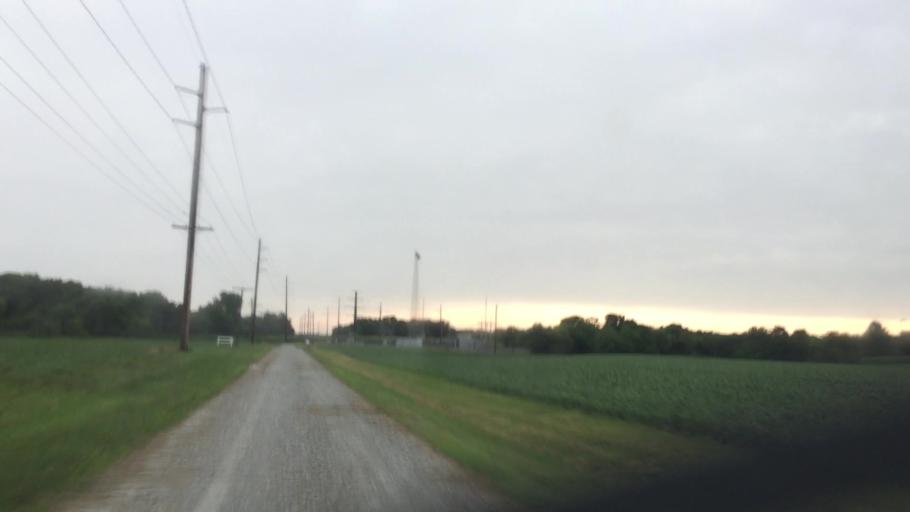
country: US
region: Iowa
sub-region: Lee County
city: Fort Madison
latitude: 40.6036
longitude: -91.2676
